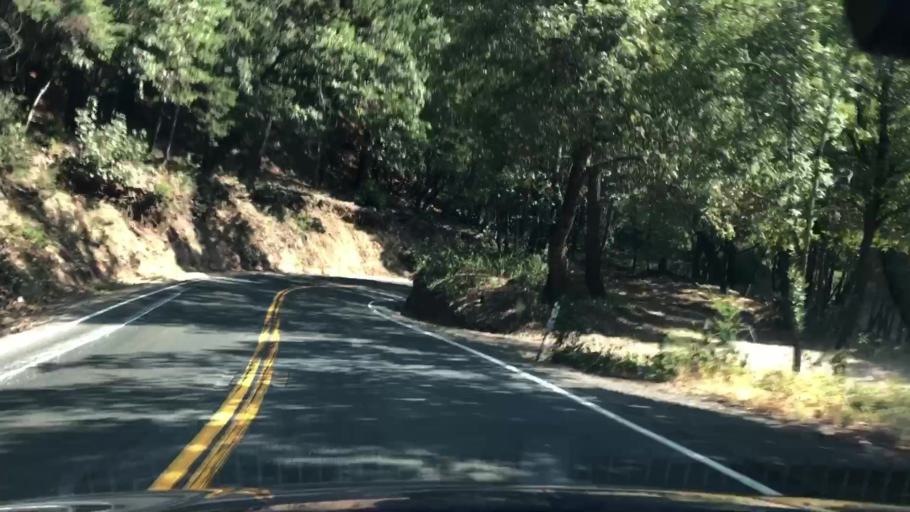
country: US
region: California
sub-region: Napa County
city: Calistoga
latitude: 38.6414
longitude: -122.5927
